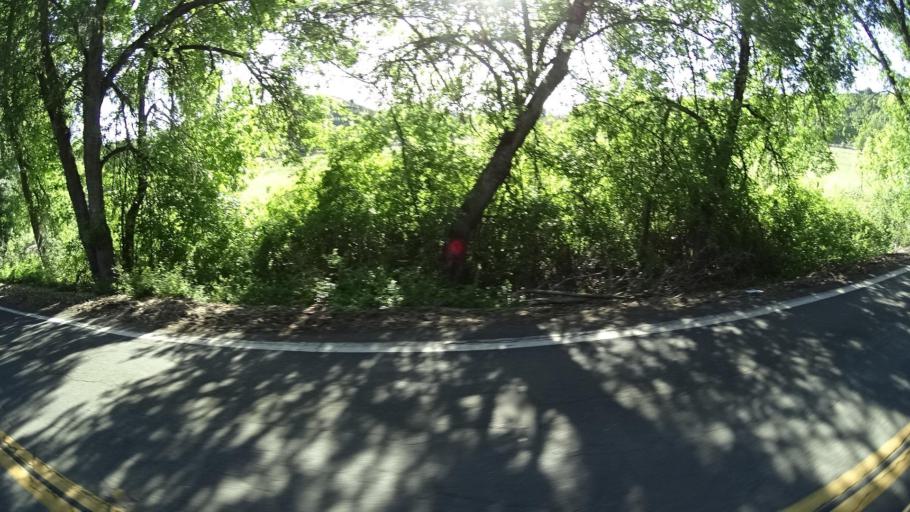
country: US
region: California
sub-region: Lake County
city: North Lakeport
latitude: 39.0926
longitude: -122.9592
